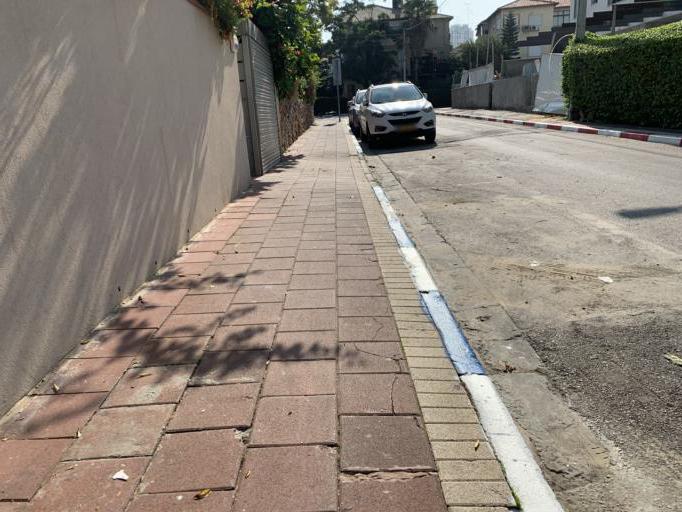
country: IL
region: Tel Aviv
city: Ramat Gan
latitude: 32.0917
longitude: 34.8112
